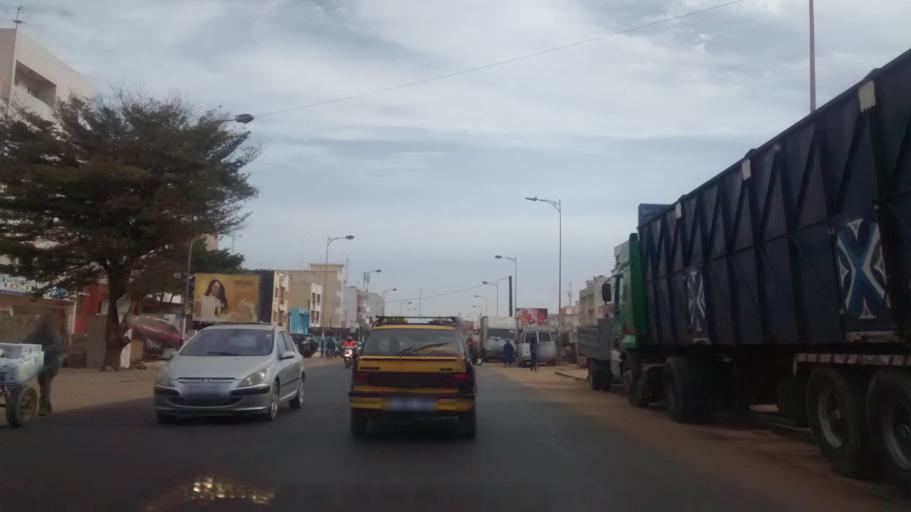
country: SN
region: Dakar
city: Pikine
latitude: 14.7547
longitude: -17.4322
